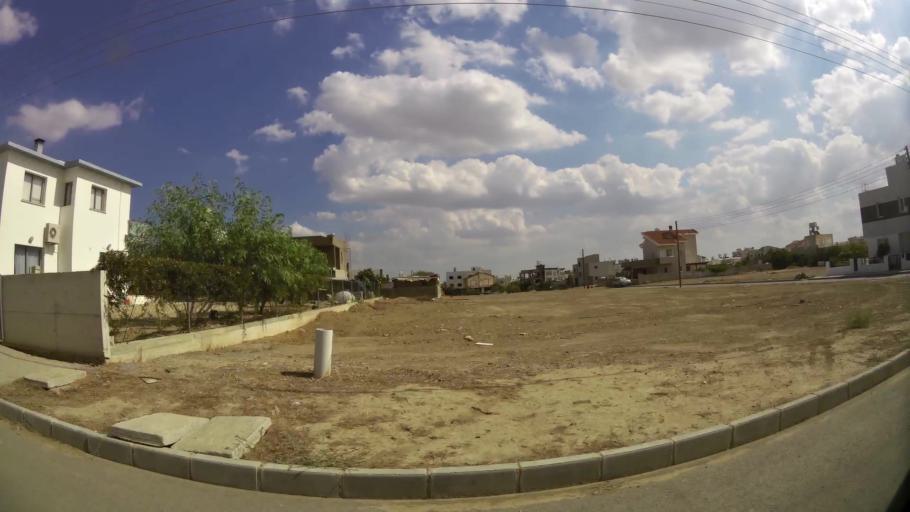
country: CY
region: Lefkosia
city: Nicosia
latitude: 35.2180
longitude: 33.2921
